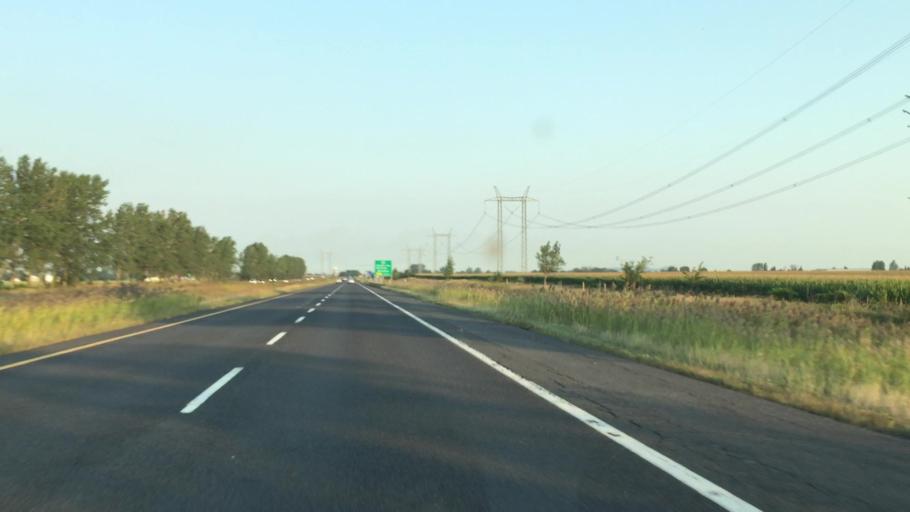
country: CA
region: Quebec
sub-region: Monteregie
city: Marieville
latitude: 45.4091
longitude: -73.2037
